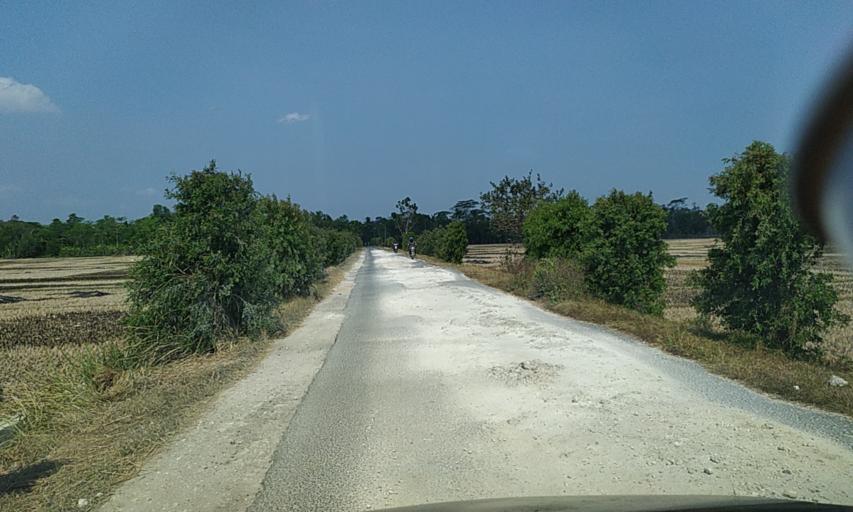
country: ID
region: Central Java
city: Ciklapa
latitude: -7.5037
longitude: 108.7976
